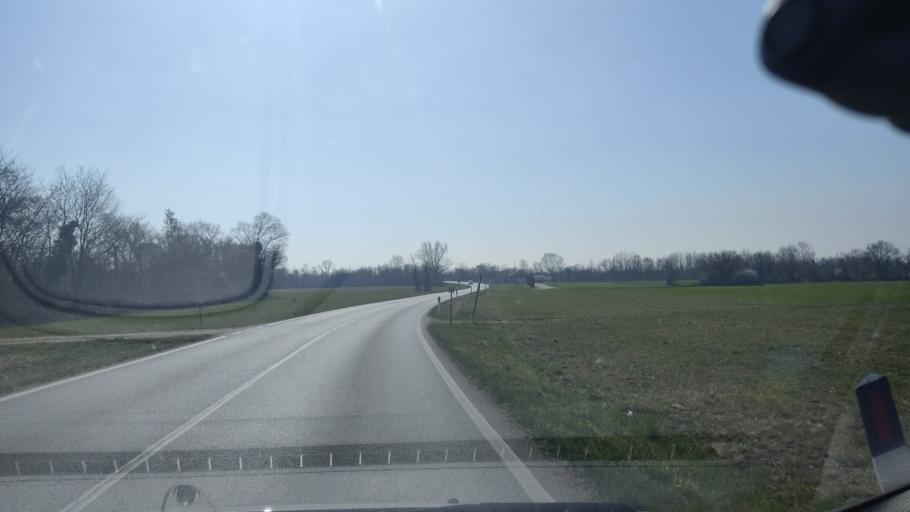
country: IT
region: Friuli Venezia Giulia
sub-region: Provincia di Pordenone
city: Budoia
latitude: 46.0340
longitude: 12.5503
